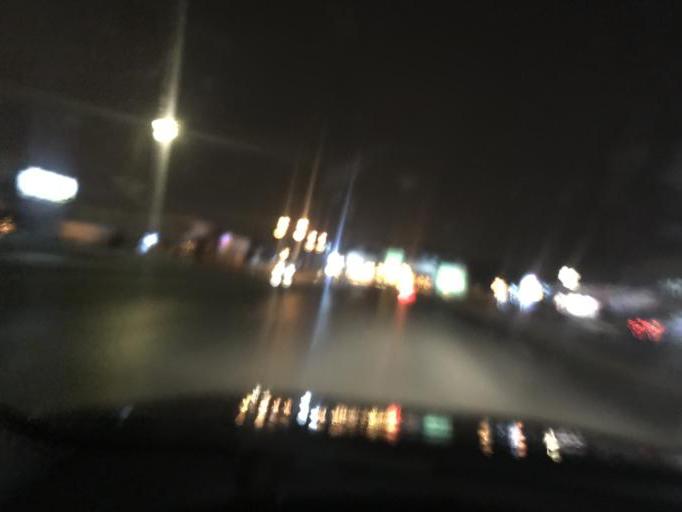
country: SA
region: Ar Riyad
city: Riyadh
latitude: 24.7987
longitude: 46.6976
